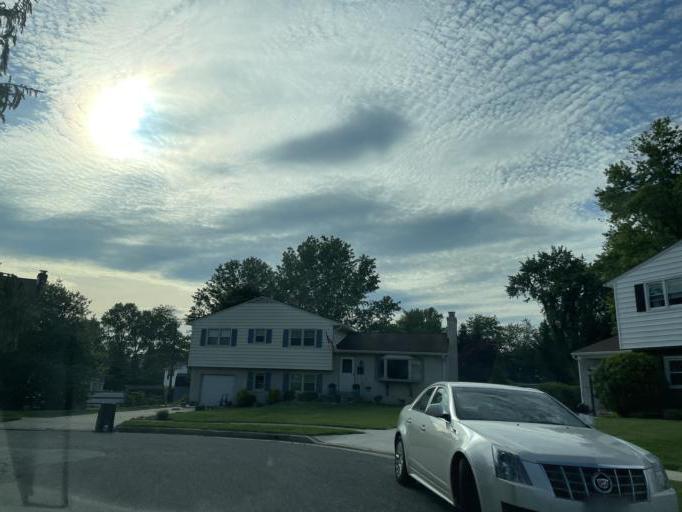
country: US
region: Maryland
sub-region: Baltimore County
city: Mays Chapel
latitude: 39.4238
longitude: -76.6473
